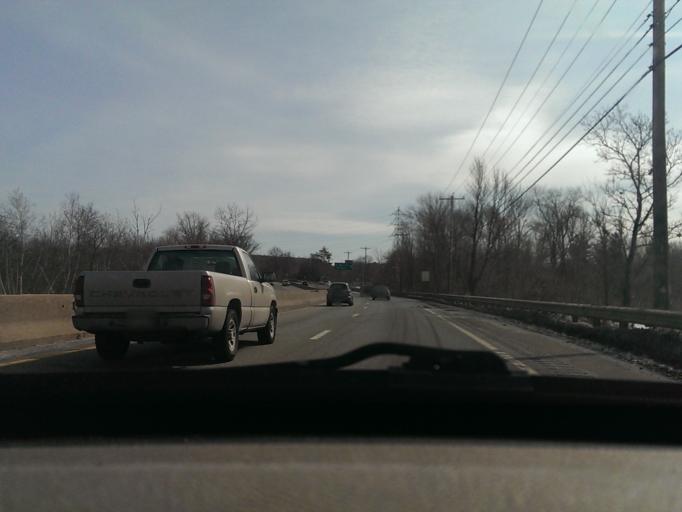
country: US
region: Massachusetts
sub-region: Worcester County
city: Millbury
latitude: 42.1900
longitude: -71.7690
